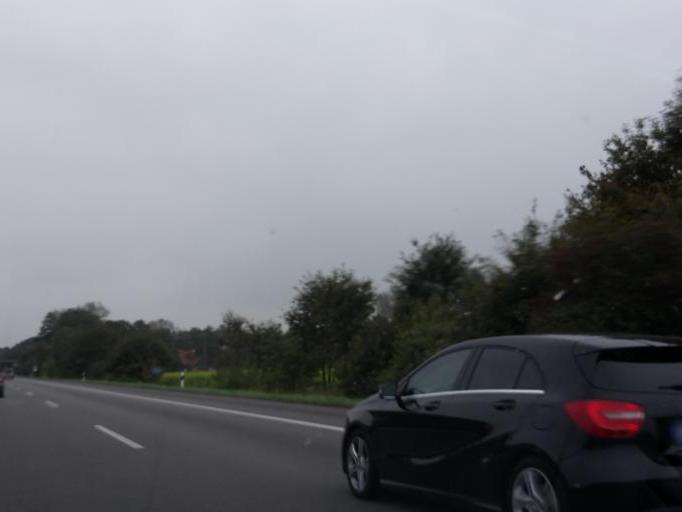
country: DE
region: Lower Saxony
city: Rieste
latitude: 52.4473
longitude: 8.0386
